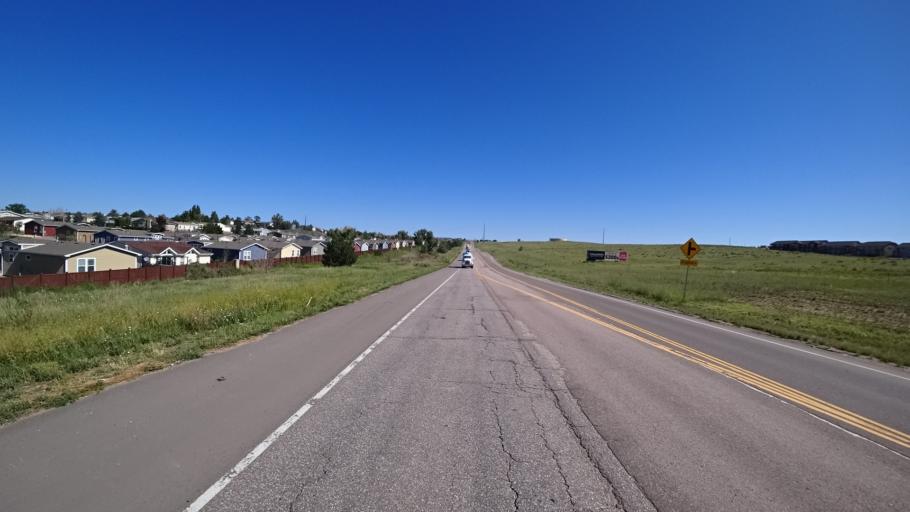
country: US
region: Colorado
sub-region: El Paso County
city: Cimarron Hills
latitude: 38.8945
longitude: -104.6829
